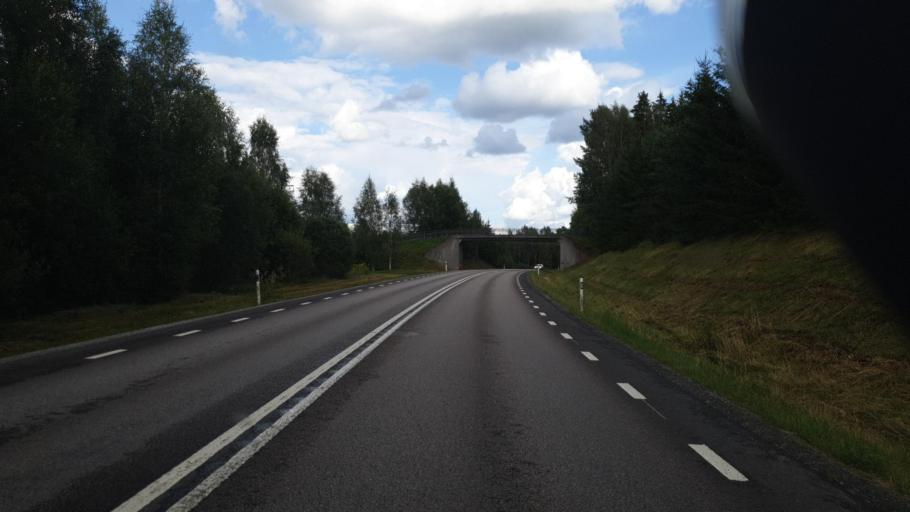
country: SE
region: Vaermland
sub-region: Arvika Kommun
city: Arvika
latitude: 59.6697
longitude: 12.5774
